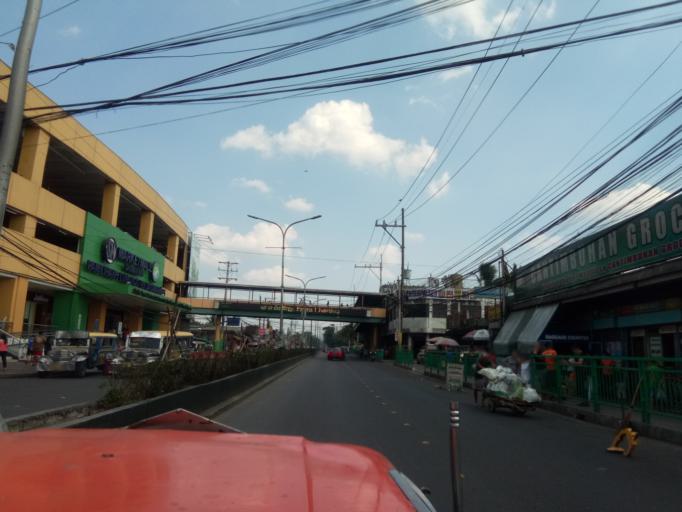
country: PH
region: Calabarzon
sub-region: Province of Cavite
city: Dasmarinas
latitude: 14.3284
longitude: 120.9592
